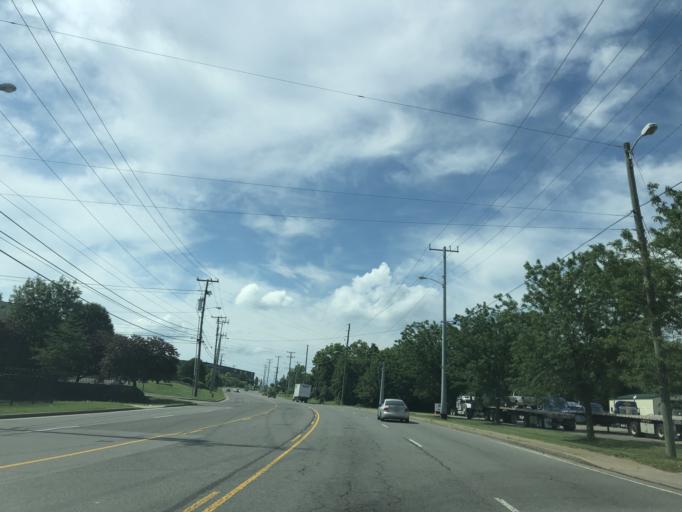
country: US
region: Tennessee
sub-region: Davidson County
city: Nashville
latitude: 36.2146
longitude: -86.7795
